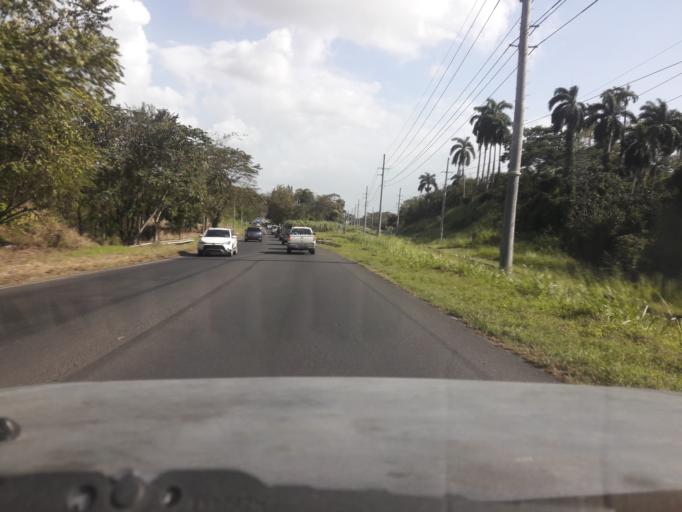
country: PA
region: Panama
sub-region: Distrito de Panama
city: Ancon
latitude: 8.9899
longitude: -79.5789
